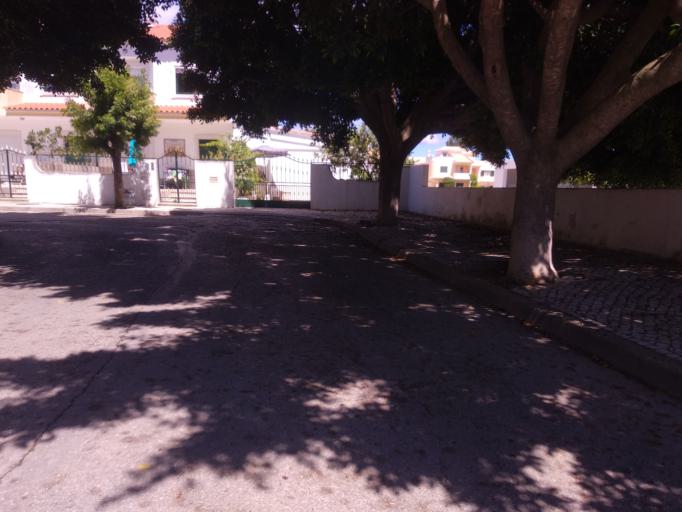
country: PT
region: Faro
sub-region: Sao Bras de Alportel
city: Sao Bras de Alportel
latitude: 37.1551
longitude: -7.8842
